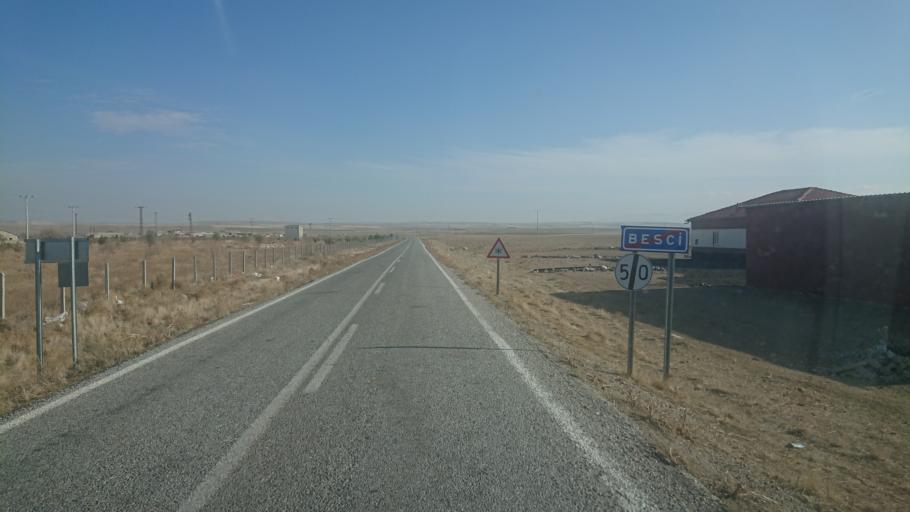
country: TR
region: Aksaray
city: Sultanhani
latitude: 38.0388
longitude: 33.5970
